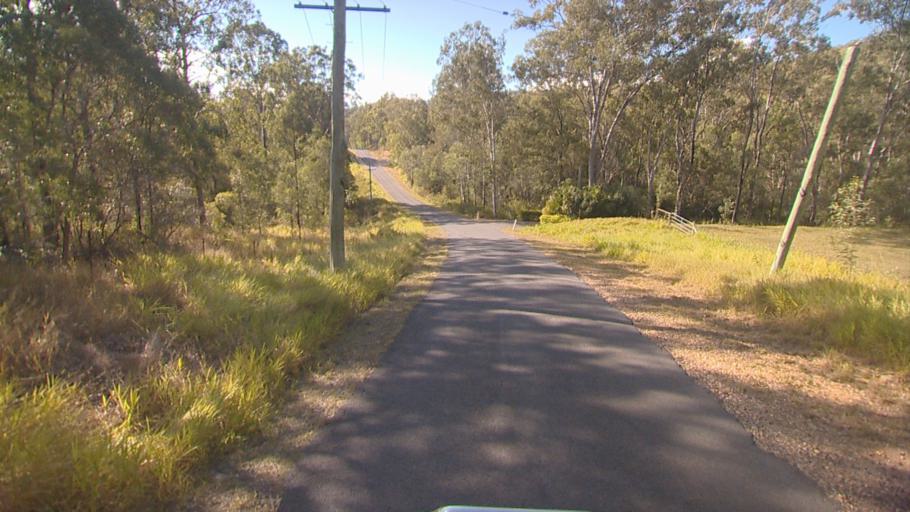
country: AU
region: Queensland
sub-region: Logan
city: Chambers Flat
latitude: -27.8247
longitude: 153.0795
